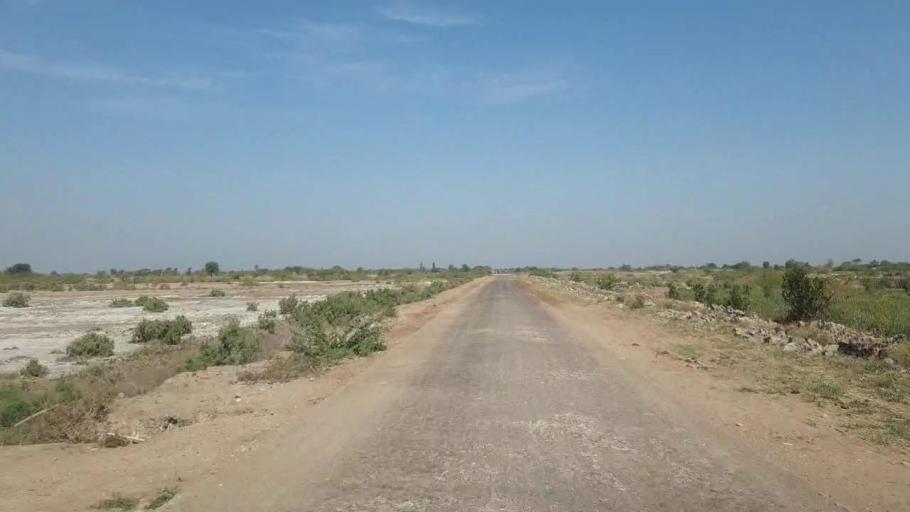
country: PK
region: Sindh
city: Samaro
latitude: 25.3757
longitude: 69.2585
